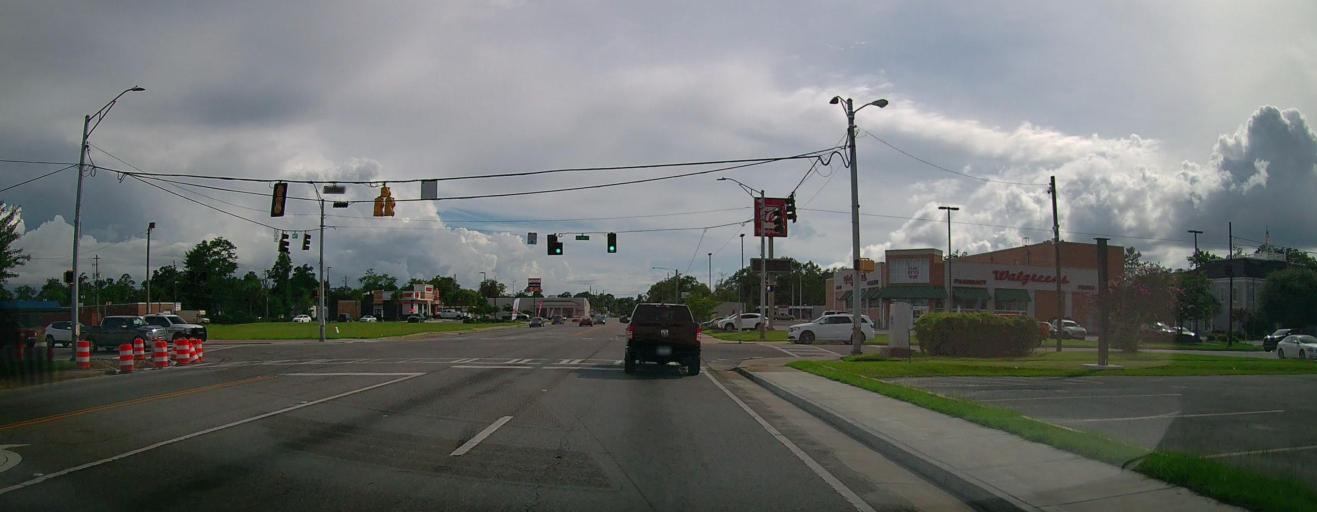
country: US
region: Georgia
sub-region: Wayne County
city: Jesup
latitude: 31.6076
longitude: -81.8850
